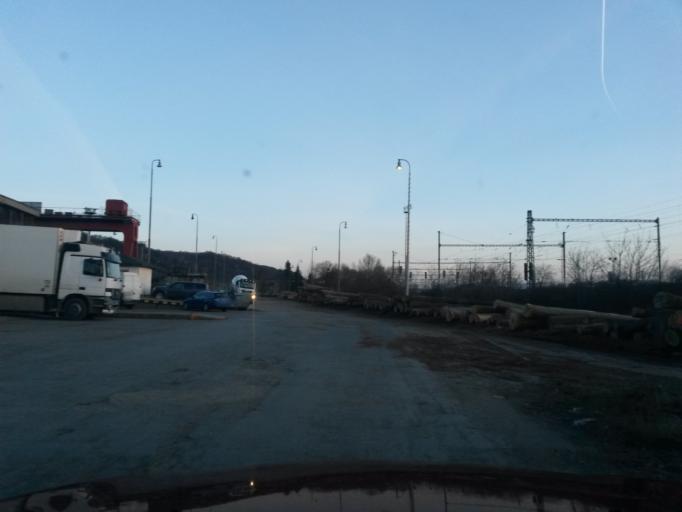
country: SK
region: Kosicky
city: Kosice
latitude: 48.7182
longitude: 21.2733
